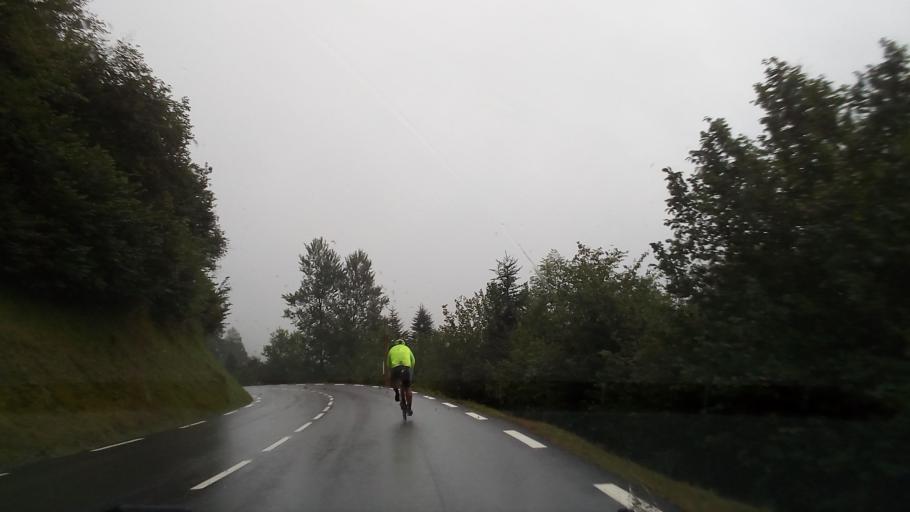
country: FR
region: Midi-Pyrenees
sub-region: Departement des Hautes-Pyrenees
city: Campan
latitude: 42.9285
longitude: 0.2009
